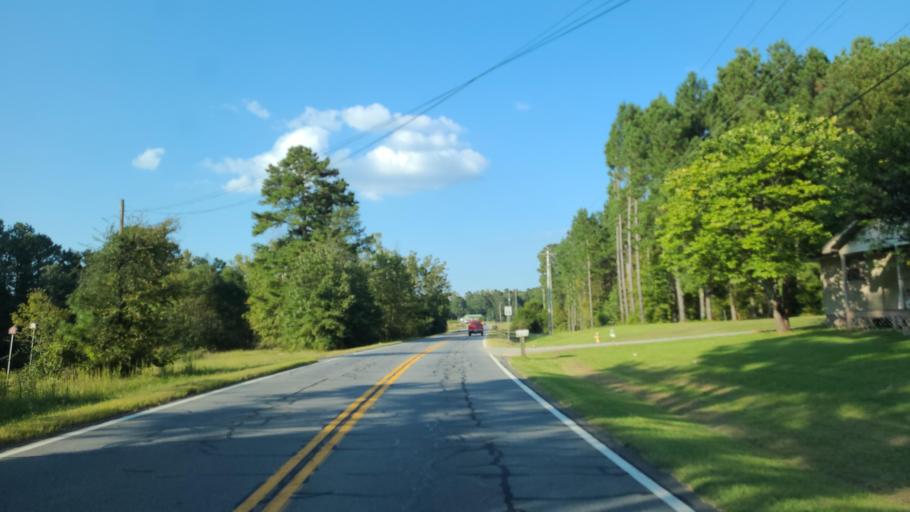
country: US
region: Georgia
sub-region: Murray County
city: Chatsworth
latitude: 34.7149
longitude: -84.8185
